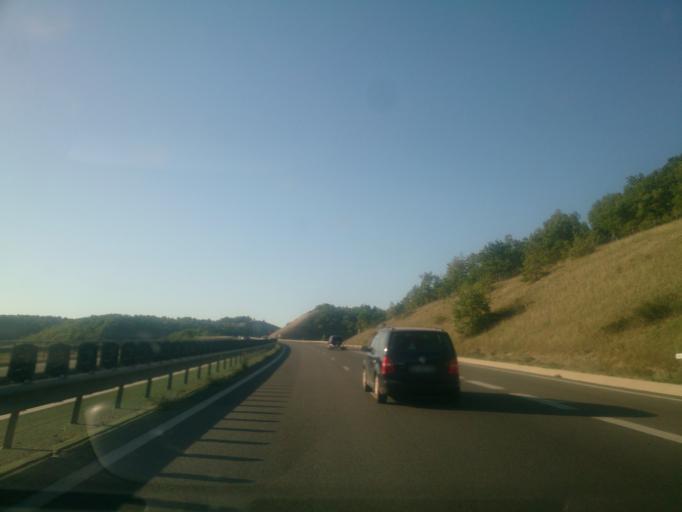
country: FR
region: Midi-Pyrenees
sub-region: Departement du Lot
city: Cahors
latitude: 44.4816
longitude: 1.5030
